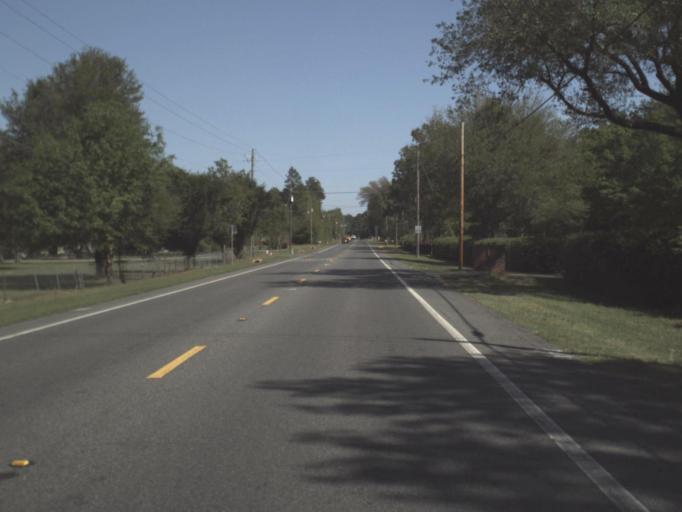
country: US
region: Florida
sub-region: Escambia County
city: Bellview
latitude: 30.5054
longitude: -87.3542
